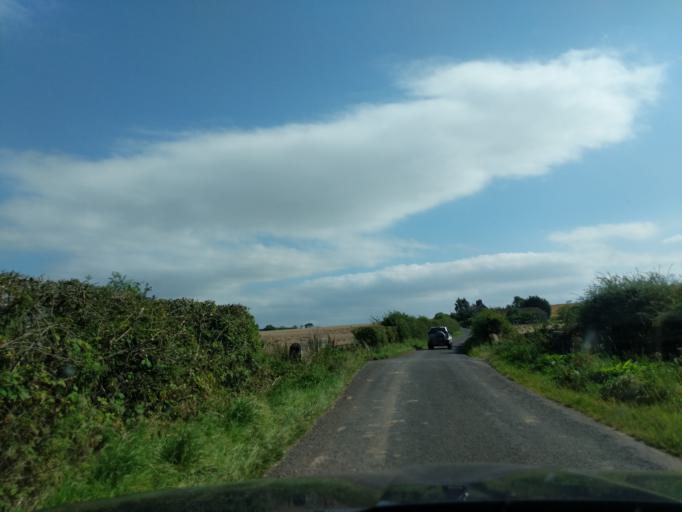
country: GB
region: England
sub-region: Northumberland
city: Ford
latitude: 55.6598
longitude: -2.1544
